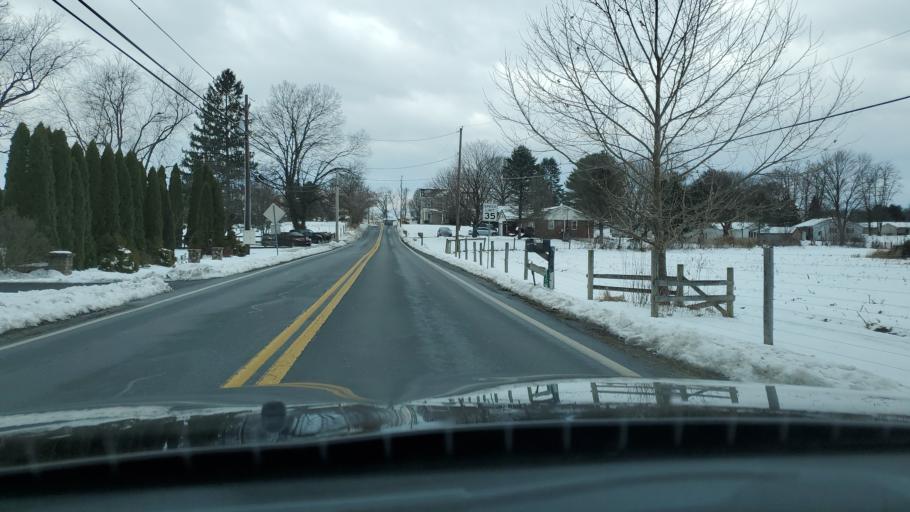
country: US
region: Pennsylvania
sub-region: Cumberland County
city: Mechanicsburg
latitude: 40.2186
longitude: -77.0481
